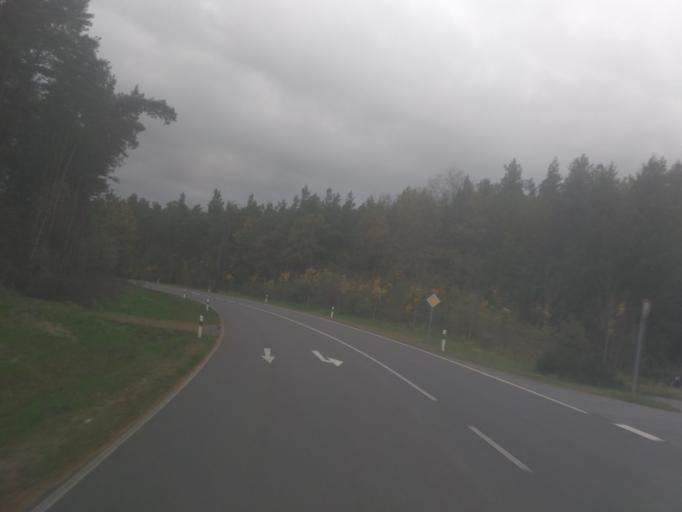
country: DE
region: Brandenburg
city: Merzdorf
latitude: 51.4021
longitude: 13.5039
